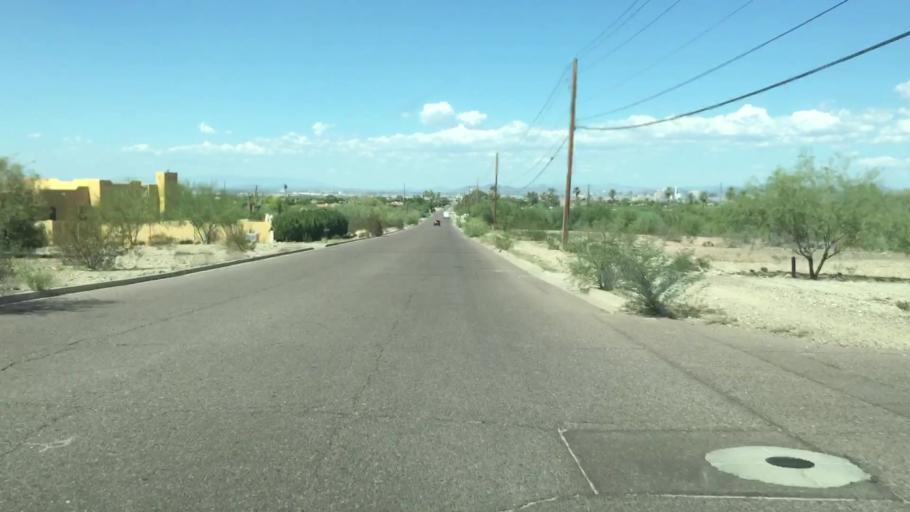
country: US
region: Arizona
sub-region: Maricopa County
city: Laveen
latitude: 33.3578
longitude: -112.1002
